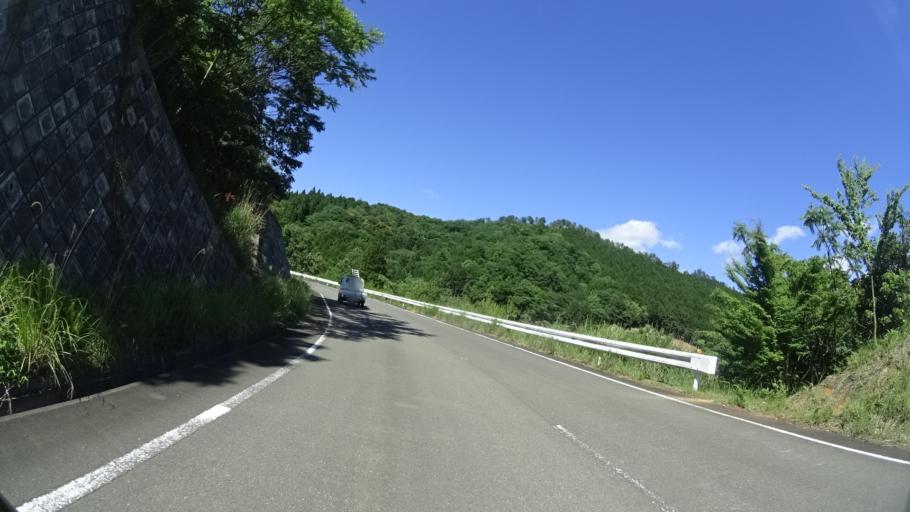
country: JP
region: Kyoto
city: Fukuchiyama
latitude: 35.3885
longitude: 135.0705
